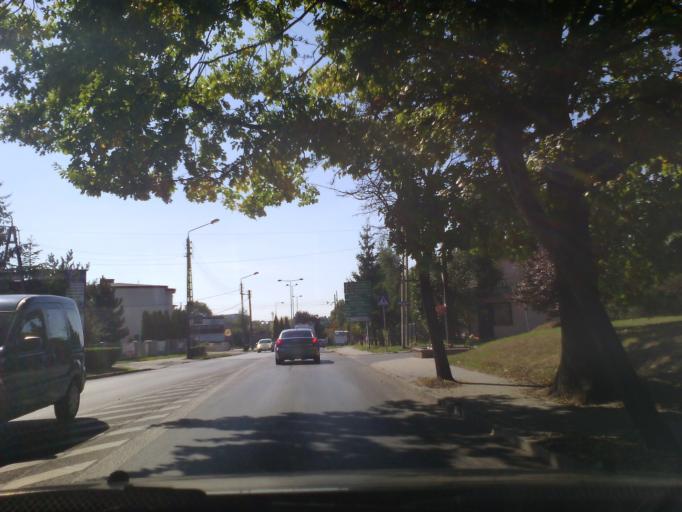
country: PL
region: Silesian Voivodeship
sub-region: Rybnik
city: Rybnik
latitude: 50.0864
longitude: 18.5300
